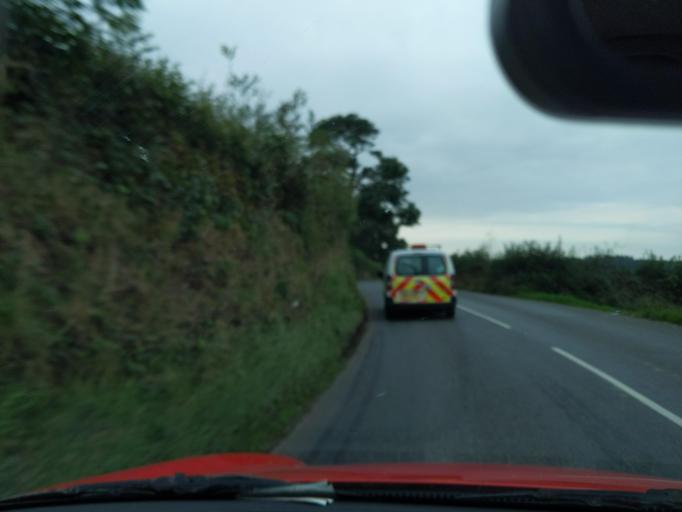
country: GB
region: England
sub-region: Devon
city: Great Torrington
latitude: 50.8680
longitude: -4.0713
